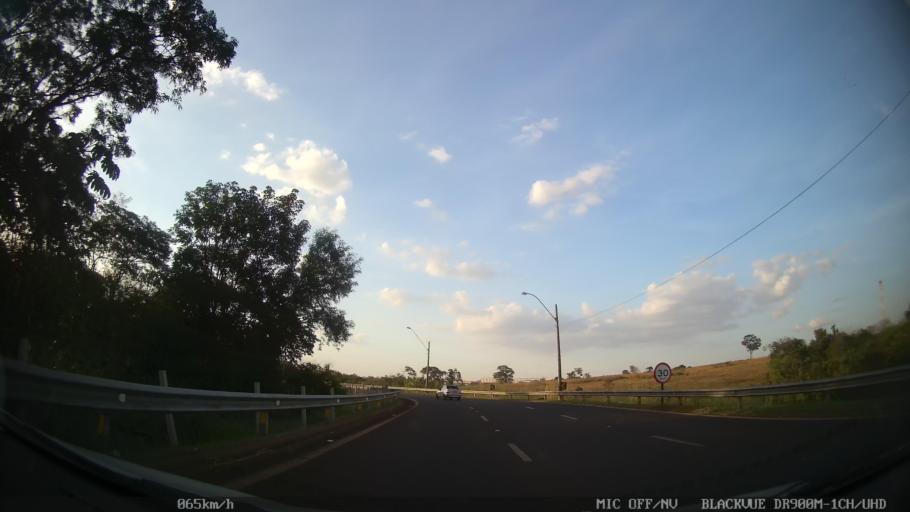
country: BR
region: Sao Paulo
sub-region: Ribeirao Preto
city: Ribeirao Preto
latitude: -21.1053
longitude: -47.8099
